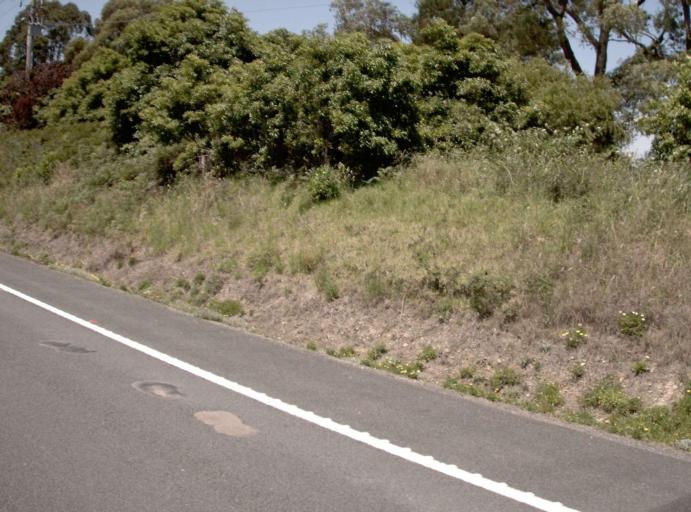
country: AU
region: Victoria
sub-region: East Gippsland
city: Lakes Entrance
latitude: -37.7046
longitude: 148.4728
